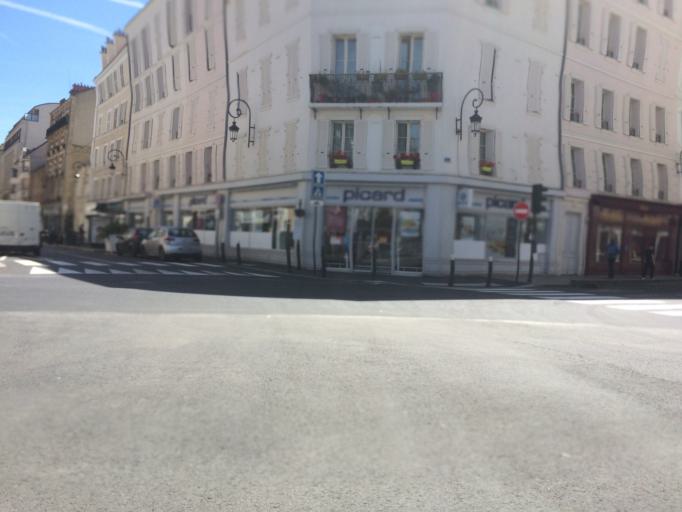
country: FR
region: Ile-de-France
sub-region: Departement des Hauts-de-Seine
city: Puteaux
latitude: 48.8826
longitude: 2.2398
